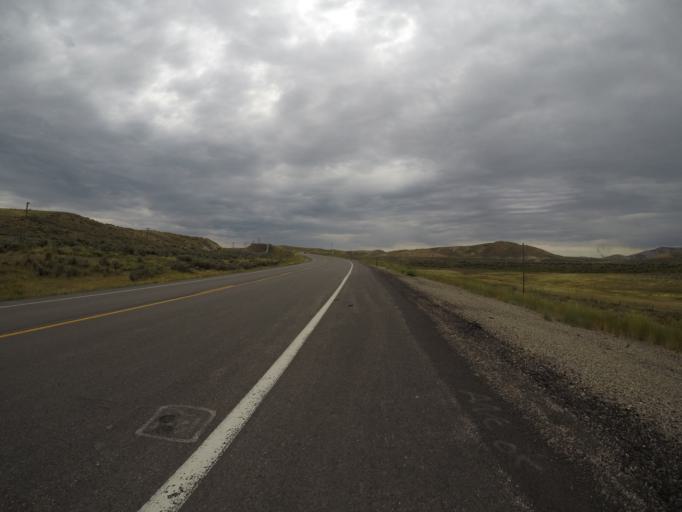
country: US
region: Wyoming
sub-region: Lincoln County
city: Kemmerer
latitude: 41.8103
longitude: -110.6190
